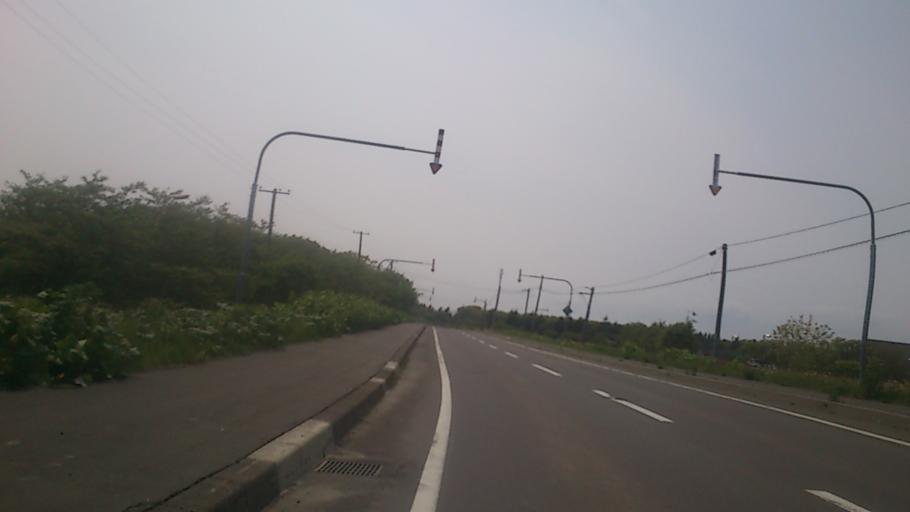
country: JP
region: Hokkaido
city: Nemuro
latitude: 43.2788
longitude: 145.5178
